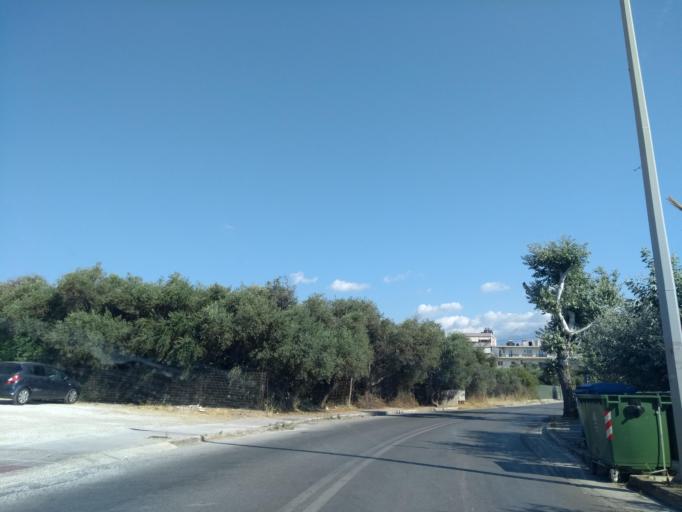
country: GR
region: Crete
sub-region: Nomos Chanias
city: Perivolia
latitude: 35.5085
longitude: 24.0036
